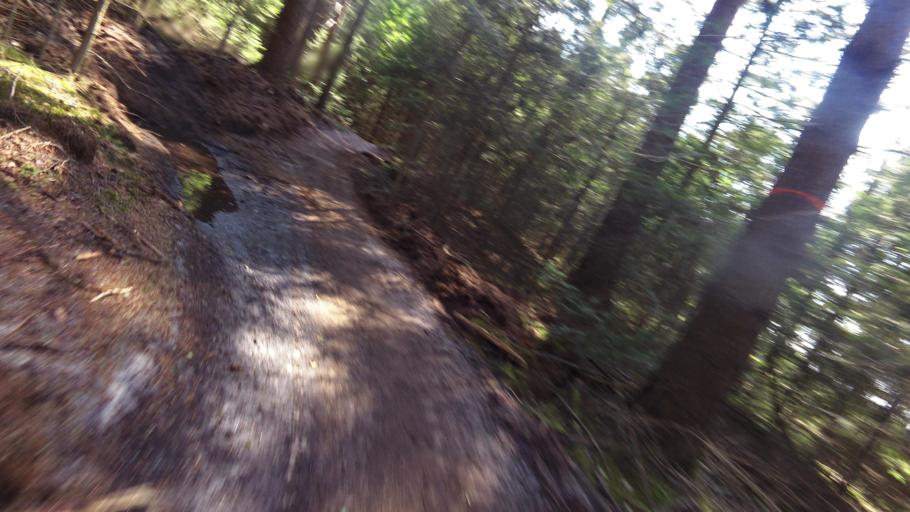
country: NL
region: Gelderland
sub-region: Gemeente Renkum
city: Oosterbeek
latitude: 52.0274
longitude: 5.8438
